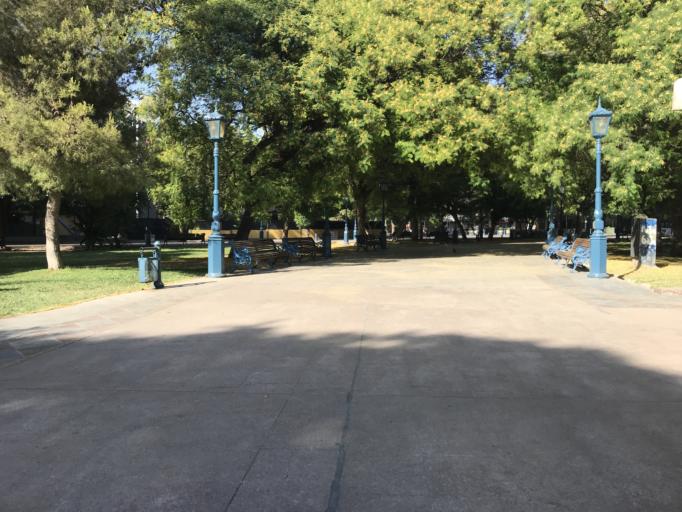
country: AR
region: Mendoza
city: Mendoza
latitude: -32.8905
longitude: -68.8439
